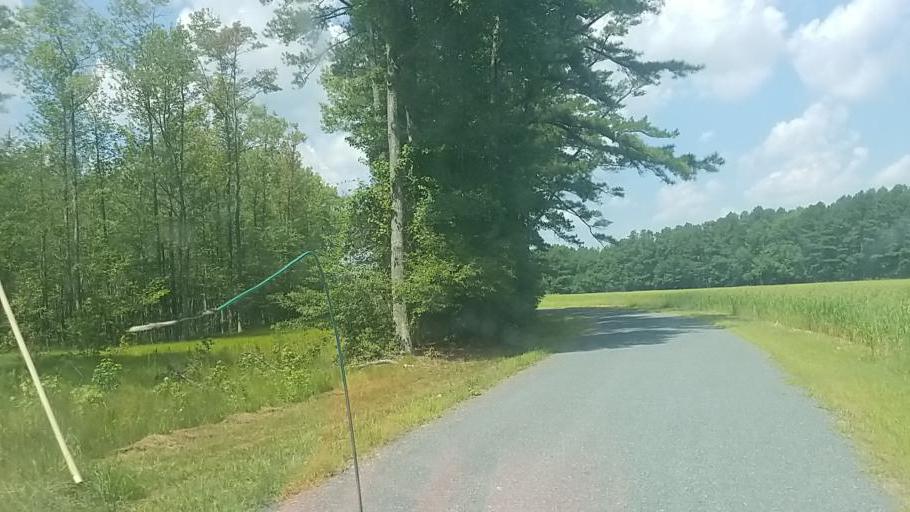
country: US
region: Maryland
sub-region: Worcester County
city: Snow Hill
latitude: 38.2498
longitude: -75.4232
